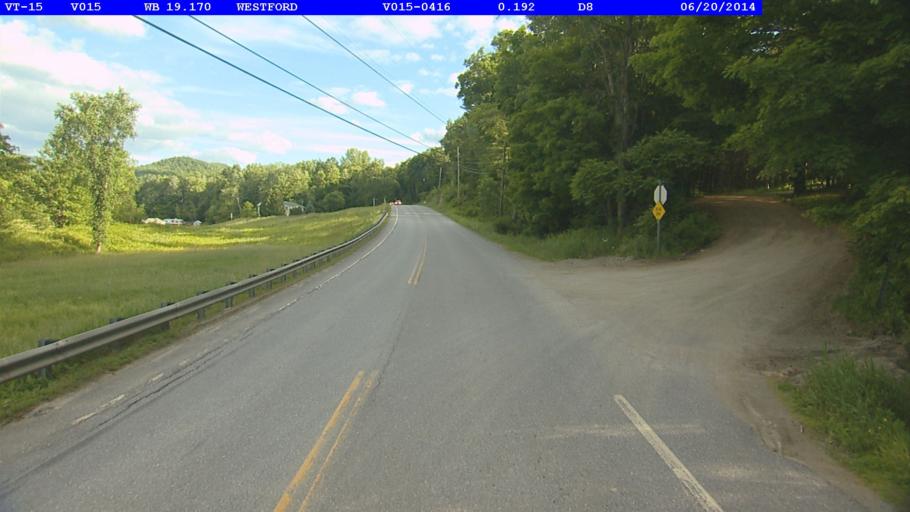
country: US
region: Vermont
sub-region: Chittenden County
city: Jericho
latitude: 44.5973
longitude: -72.9373
